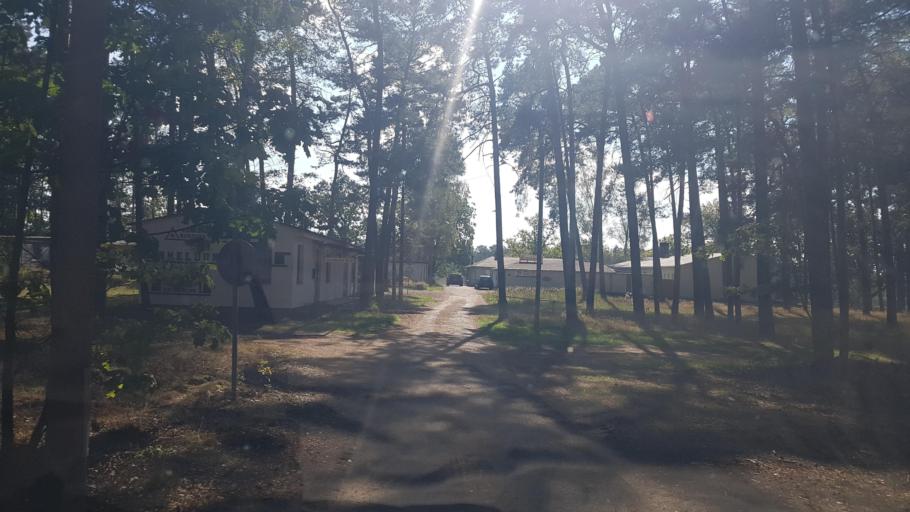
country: DE
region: Brandenburg
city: Lebusa
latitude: 51.8180
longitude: 13.4025
